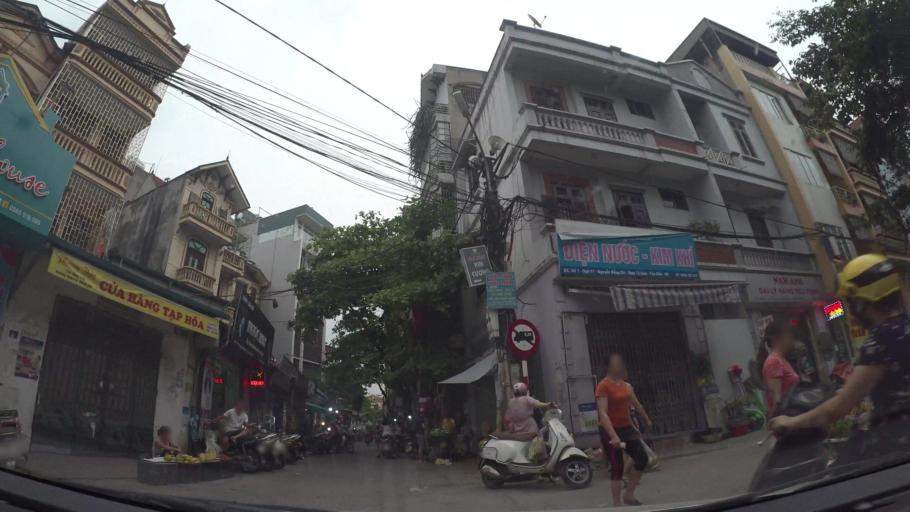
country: VN
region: Ha Noi
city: Cau Dien
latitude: 21.0361
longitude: 105.7641
